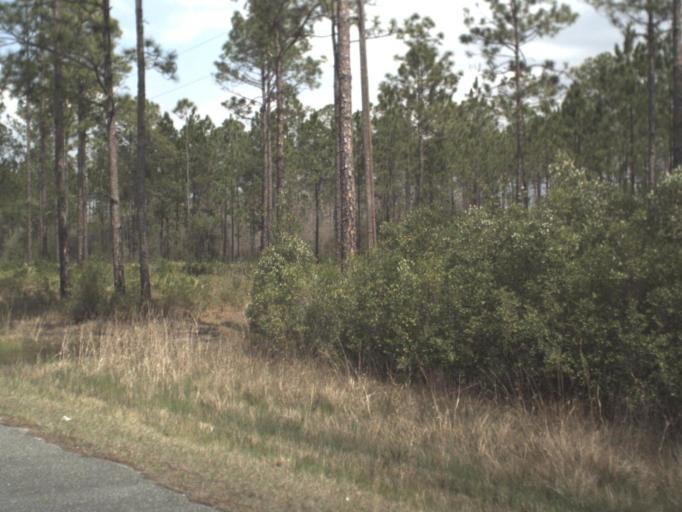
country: US
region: Florida
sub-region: Franklin County
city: Apalachicola
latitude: 29.9500
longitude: -84.9764
